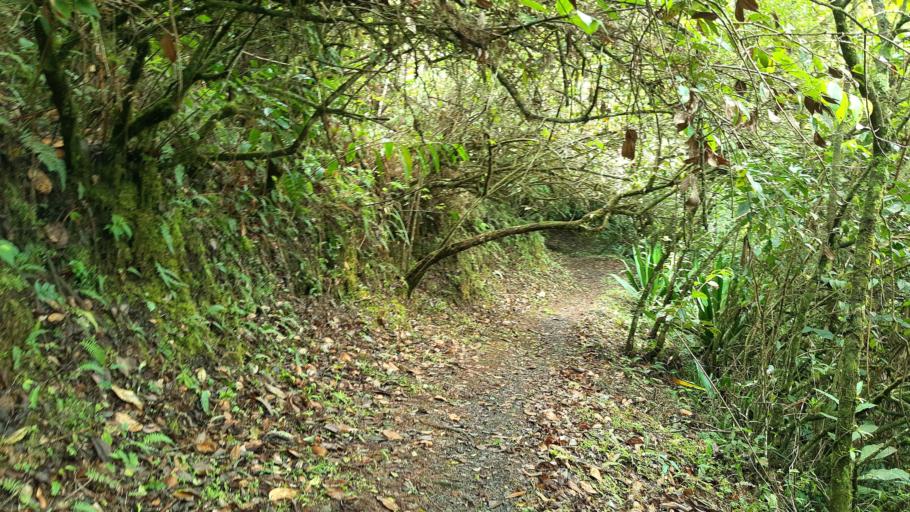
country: CO
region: Boyaca
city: Santa Maria
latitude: 4.9176
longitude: -73.3036
